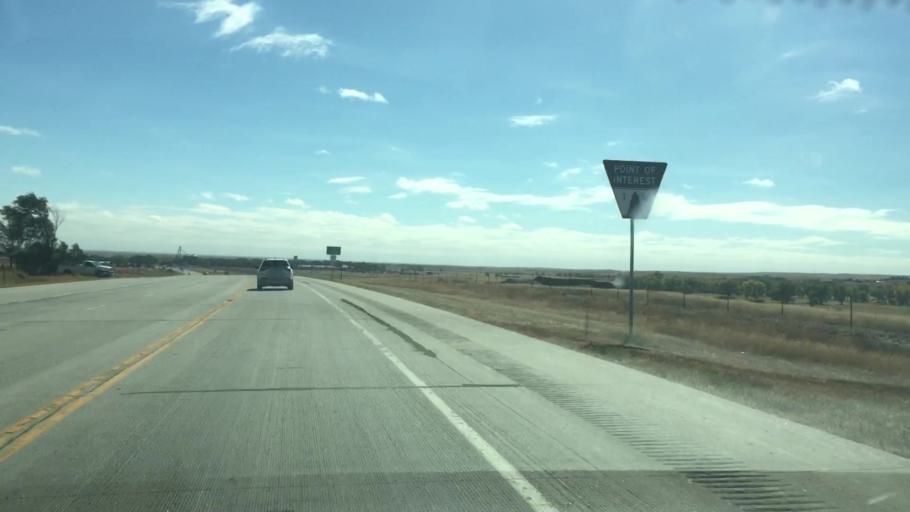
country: US
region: Colorado
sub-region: Lincoln County
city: Hugo
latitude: 39.1426
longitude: -103.4902
